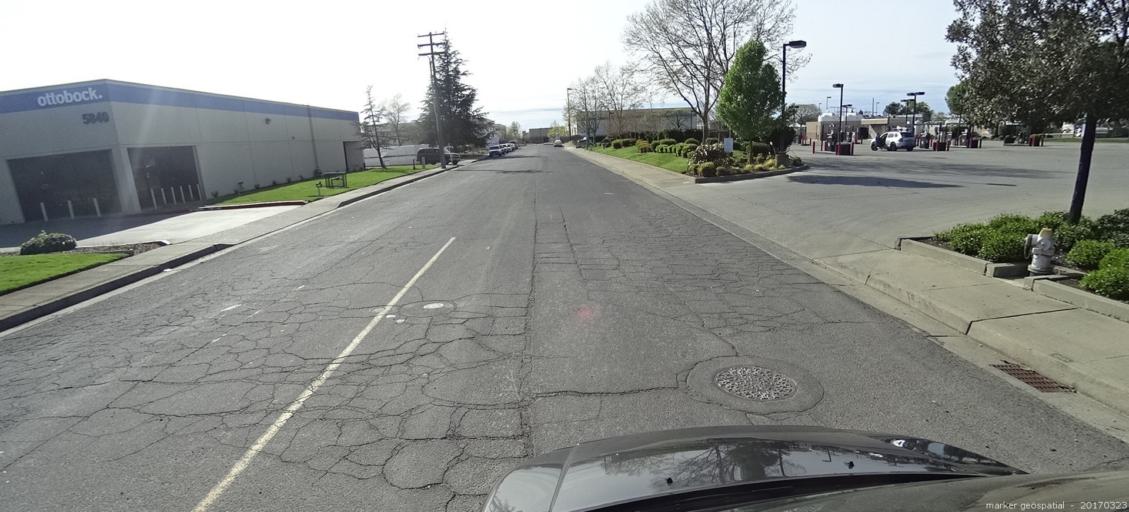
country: US
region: California
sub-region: Sacramento County
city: Rosemont
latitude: 38.5221
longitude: -121.3702
